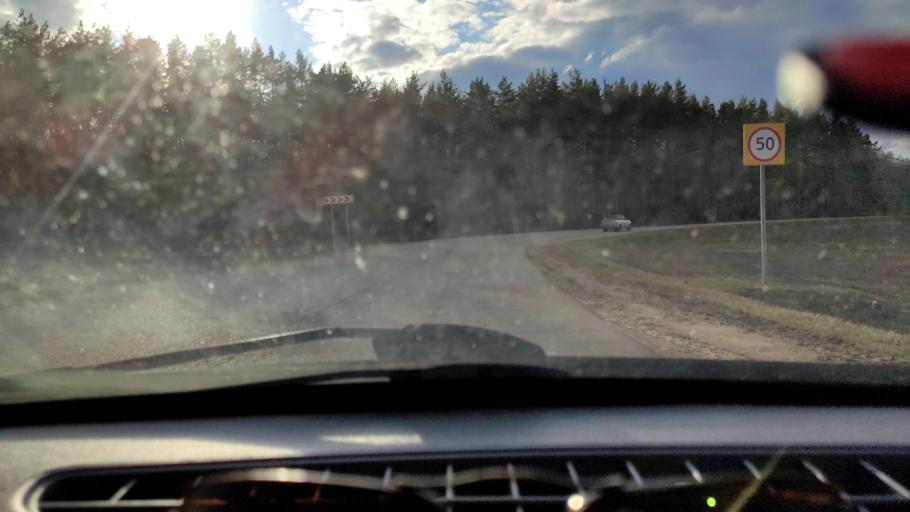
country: RU
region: Bashkortostan
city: Karmaskaly
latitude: 54.3422
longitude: 56.0928
